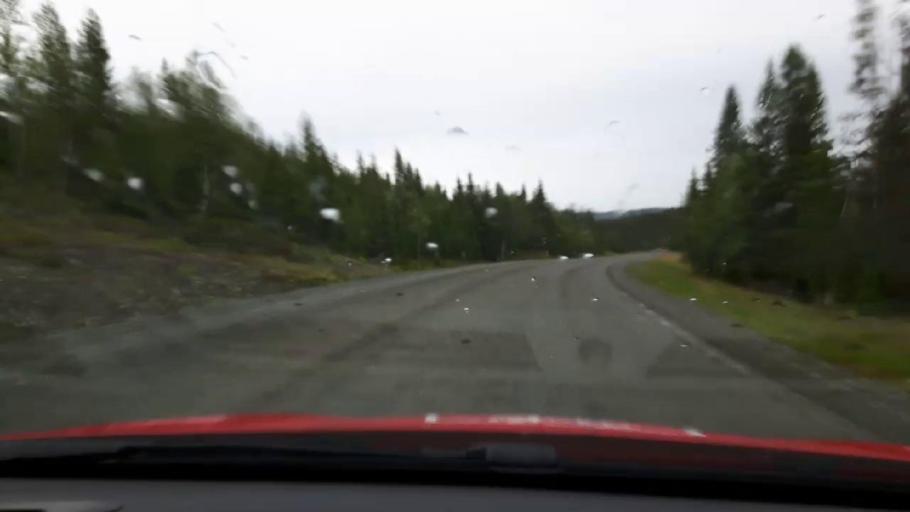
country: SE
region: Jaemtland
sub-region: Are Kommun
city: Are
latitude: 63.4143
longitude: 12.7671
